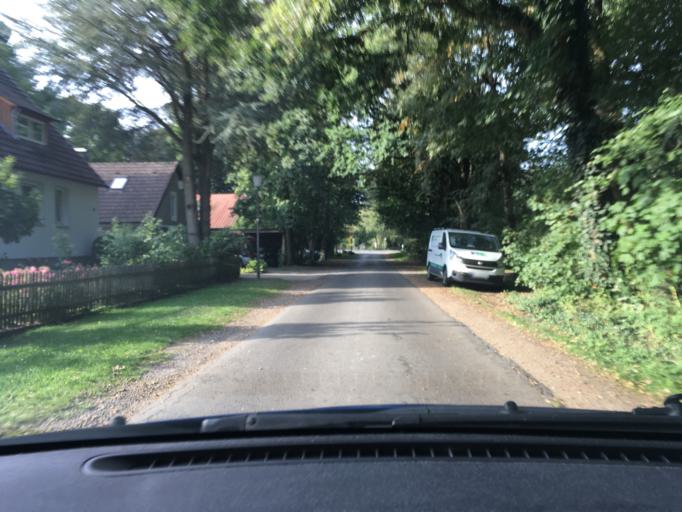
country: DE
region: Lower Saxony
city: Fassberg
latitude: 52.8961
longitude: 10.1237
